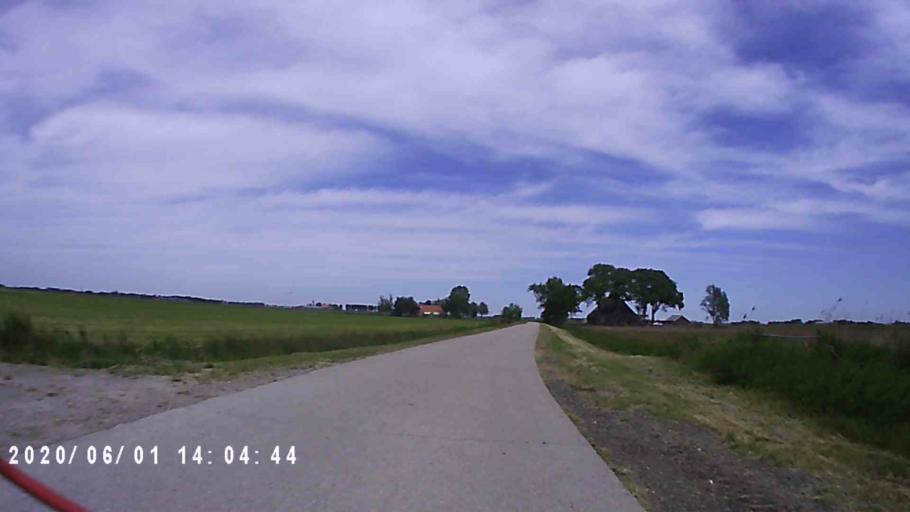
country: NL
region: Friesland
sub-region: Gemeente Littenseradiel
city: Winsum
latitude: 53.1148
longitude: 5.6328
